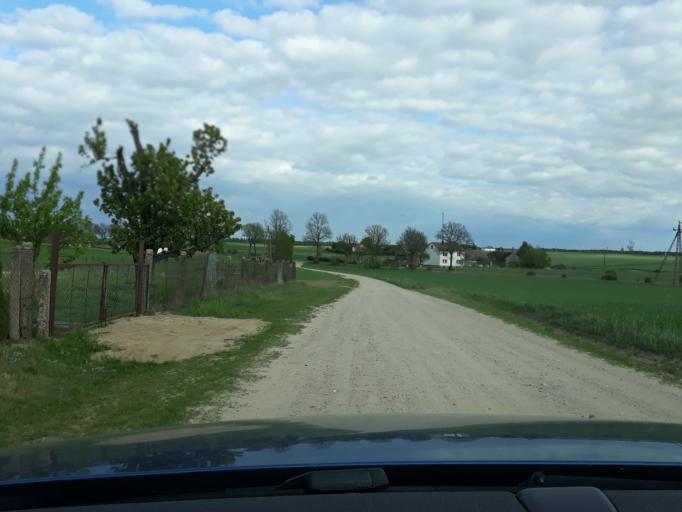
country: PL
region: Pomeranian Voivodeship
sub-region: Powiat czluchowski
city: Czluchow
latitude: 53.7530
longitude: 17.3739
